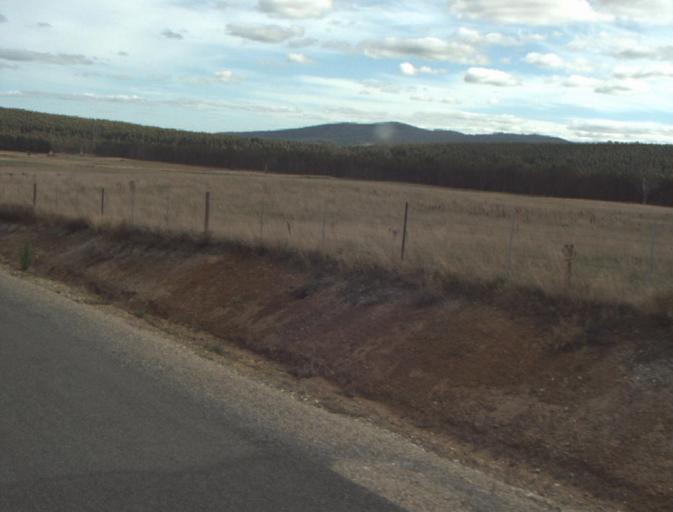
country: AU
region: Tasmania
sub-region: Launceston
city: Mayfield
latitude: -41.2024
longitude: 147.1892
